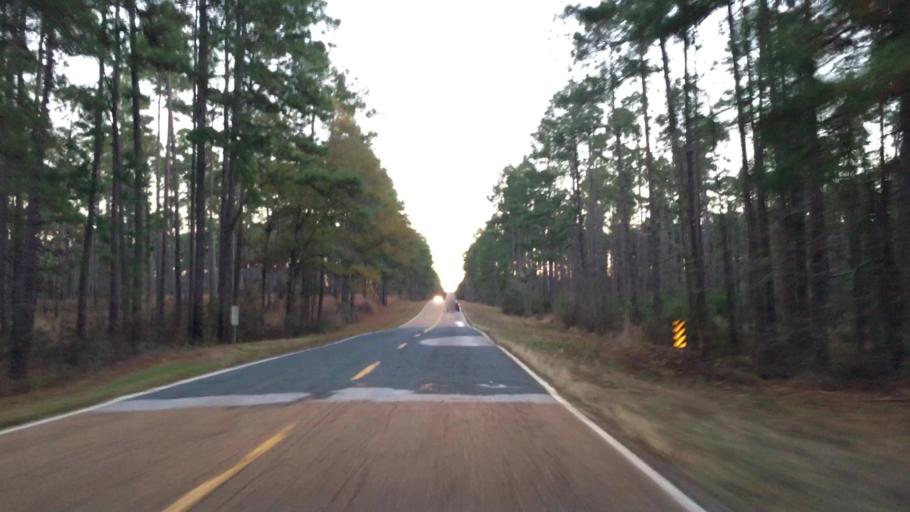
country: US
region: Louisiana
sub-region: Vernon Parish
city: Fort Polk South
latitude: 31.0097
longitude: -93.1855
